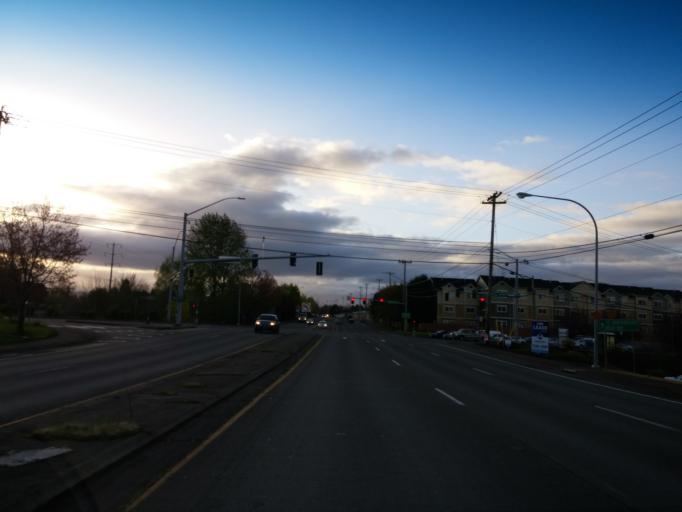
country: US
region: Oregon
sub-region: Washington County
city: Aloha
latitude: 45.5158
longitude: -122.8683
